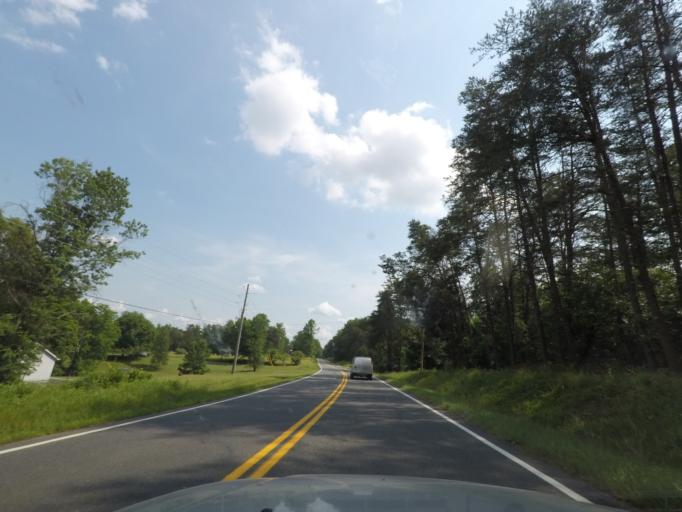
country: US
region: Virginia
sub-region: Fluvanna County
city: Palmyra
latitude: 37.8881
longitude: -78.2631
